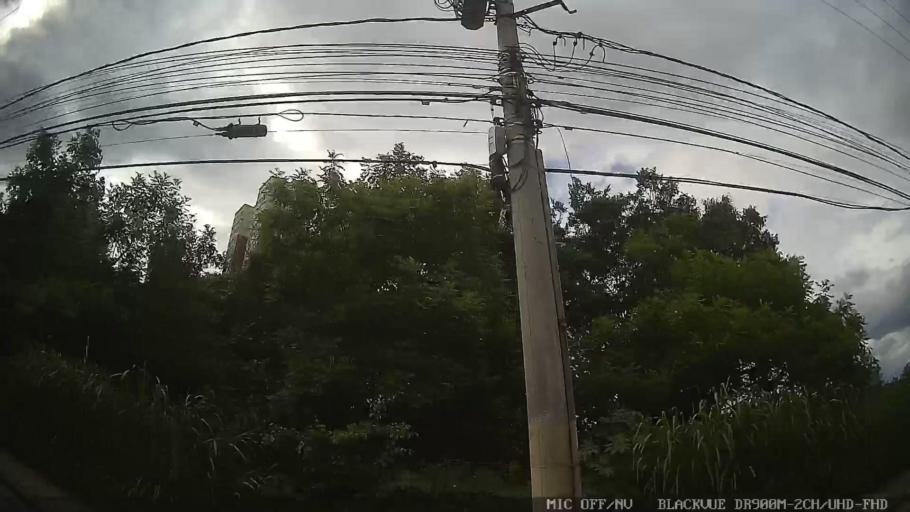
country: BR
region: Sao Paulo
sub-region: Mogi das Cruzes
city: Mogi das Cruzes
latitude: -23.5160
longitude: -46.1723
